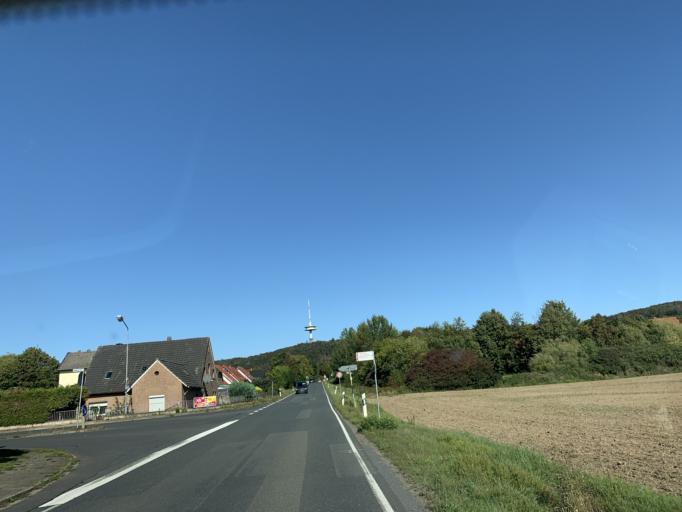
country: DE
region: North Rhine-Westphalia
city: Porta Westfalica
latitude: 52.2293
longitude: 8.9437
